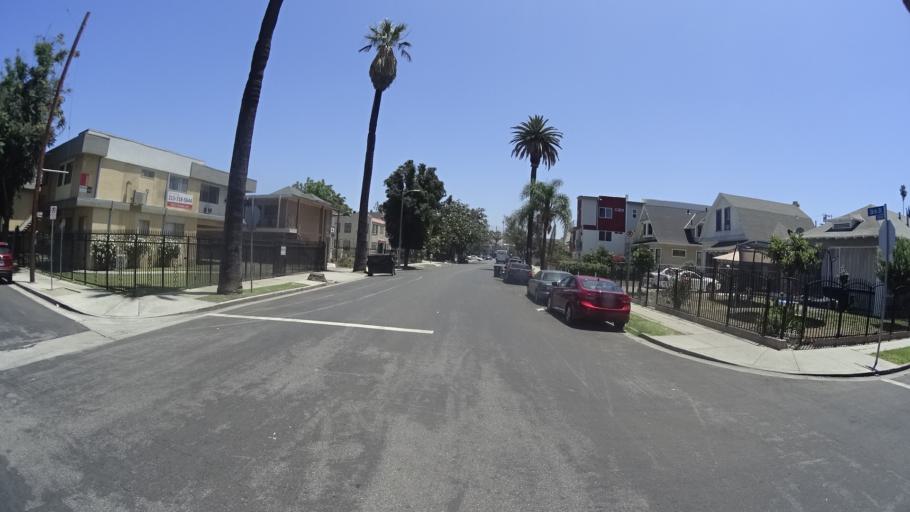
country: US
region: California
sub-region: Los Angeles County
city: Los Angeles
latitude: 34.0231
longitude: -118.2938
